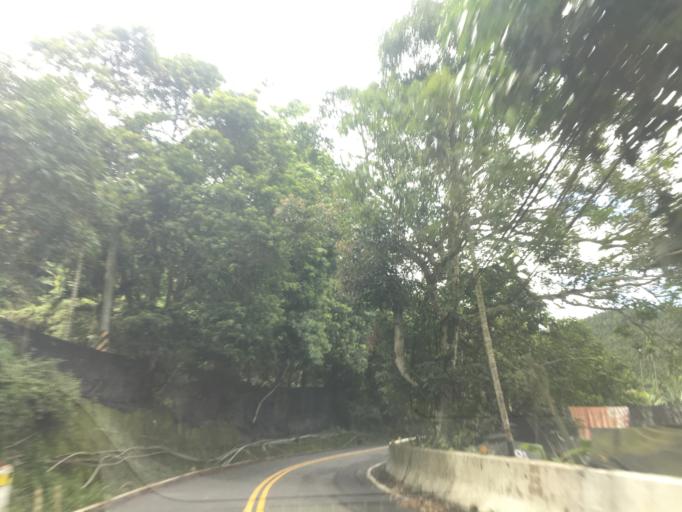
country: TW
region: Taiwan
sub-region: Yunlin
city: Douliu
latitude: 23.5659
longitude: 120.5740
